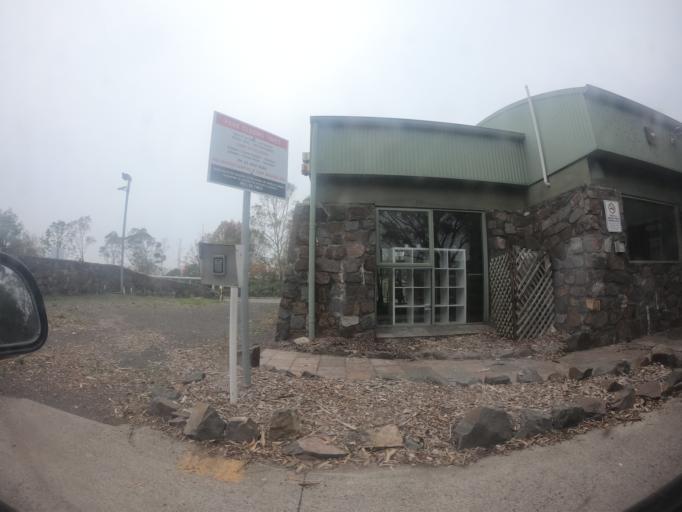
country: AU
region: New South Wales
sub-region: Shellharbour
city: Flinders
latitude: -34.6005
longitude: 150.8596
